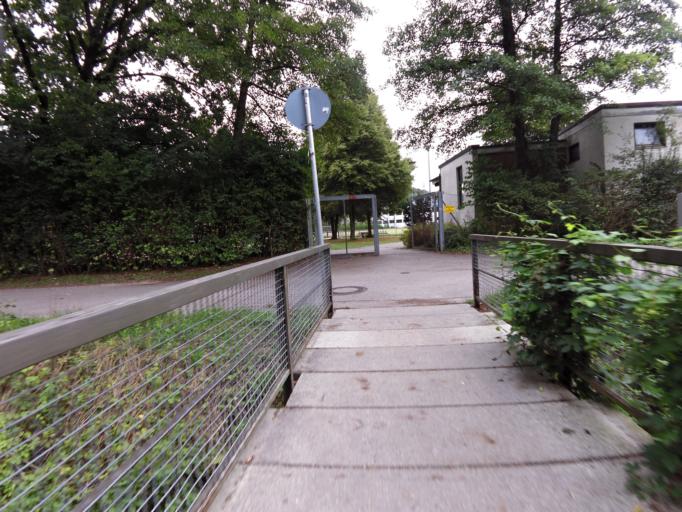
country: DE
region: Bavaria
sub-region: Lower Bavaria
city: Landshut
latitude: 48.5308
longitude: 12.1362
